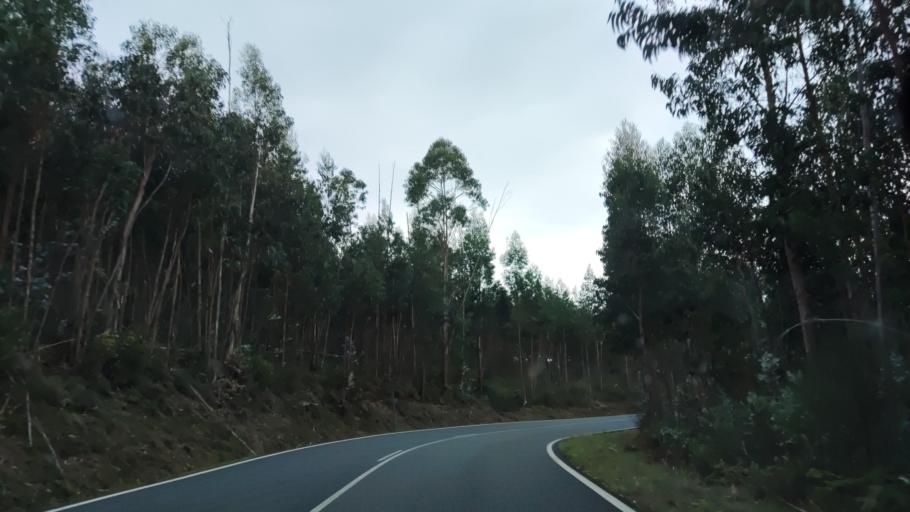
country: ES
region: Galicia
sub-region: Provincia de Pontevedra
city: Catoira
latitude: 42.6529
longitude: -8.7574
